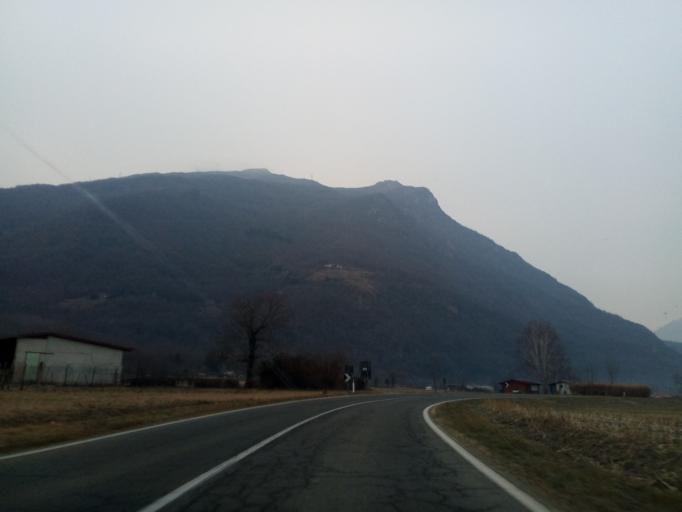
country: IT
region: Piedmont
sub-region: Provincia di Torino
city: Lessolo
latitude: 45.4968
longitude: 7.8288
